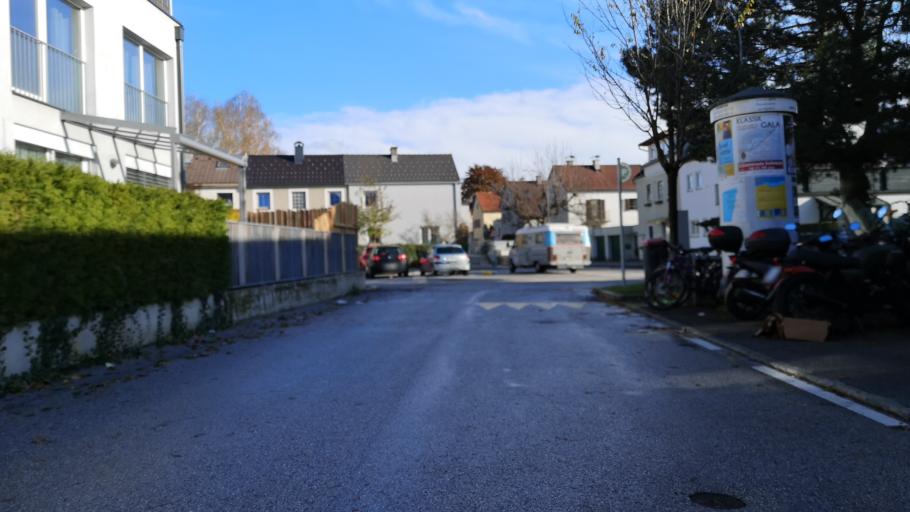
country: AT
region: Tyrol
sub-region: Innsbruck Stadt
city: Innsbruck
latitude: 47.2638
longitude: 11.3672
